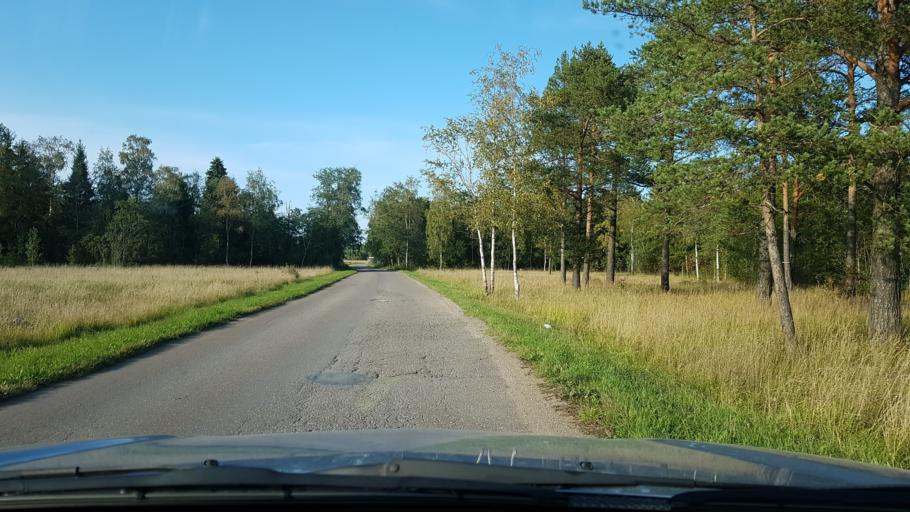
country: EE
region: Ida-Virumaa
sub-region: Narva-Joesuu linn
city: Narva-Joesuu
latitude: 59.3841
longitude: 28.0875
